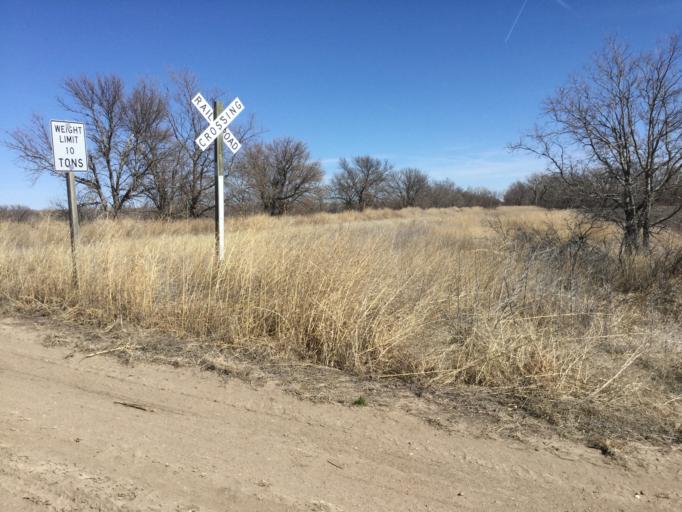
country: US
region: Kansas
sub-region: Rawlins County
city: Atwood
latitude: 39.8963
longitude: -100.8337
